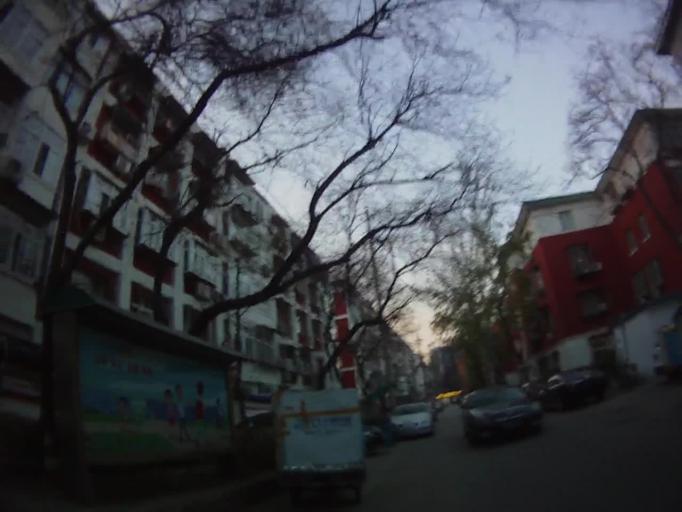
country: CN
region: Beijing
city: Longtan
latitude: 39.8861
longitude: 116.4295
